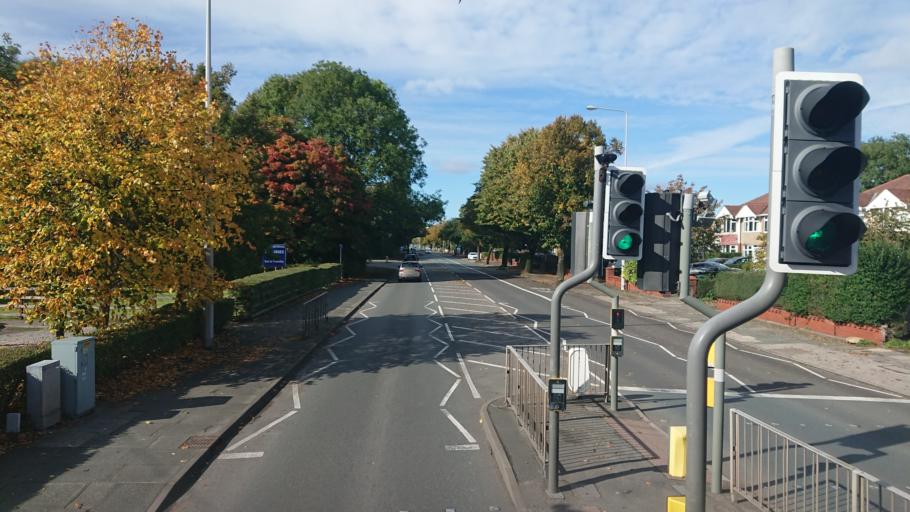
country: GB
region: England
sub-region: Lancashire
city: Lancaster
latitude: 54.0574
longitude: -2.8202
